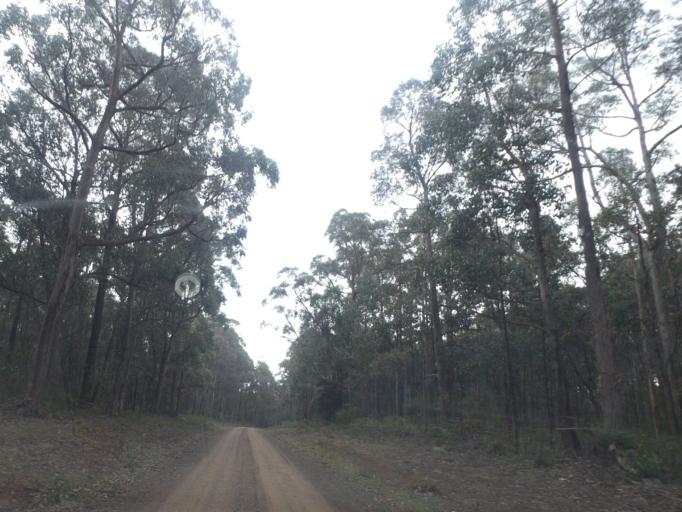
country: AU
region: Victoria
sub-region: Moorabool
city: Bacchus Marsh
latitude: -37.4224
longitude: 144.3095
